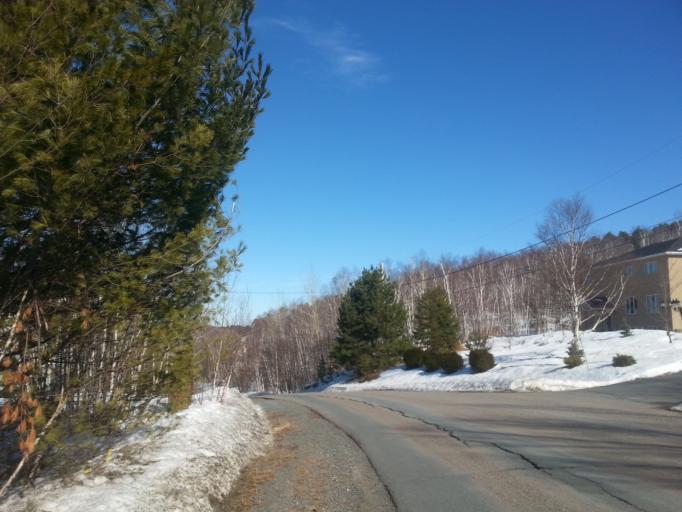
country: CA
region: Ontario
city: Greater Sudbury
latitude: 46.4035
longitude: -81.0268
